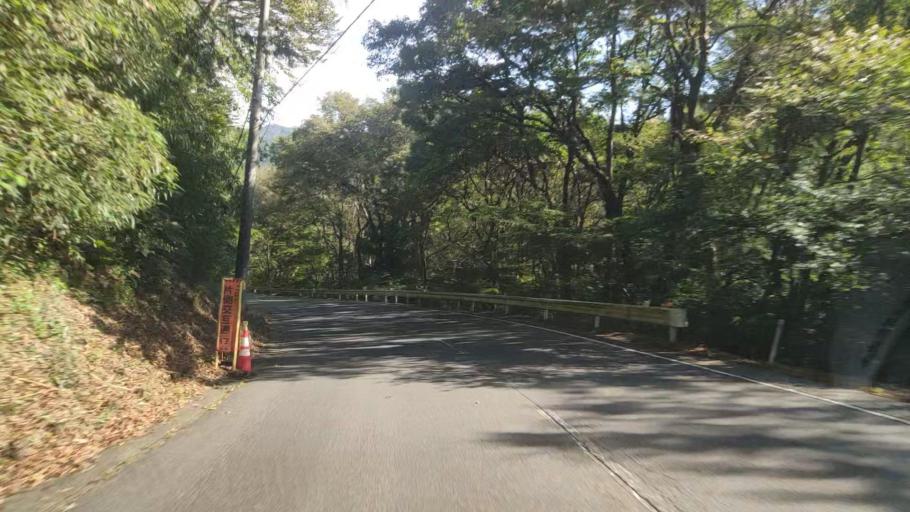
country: JP
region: Gunma
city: Nakanojomachi
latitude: 36.6131
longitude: 138.7401
